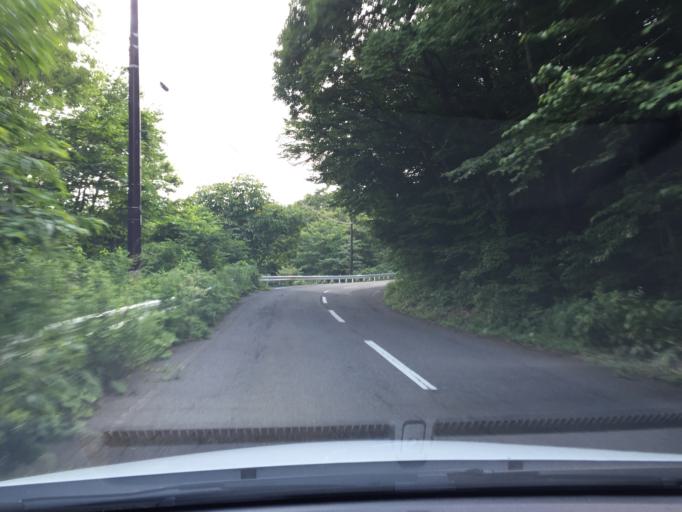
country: JP
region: Tochigi
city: Kuroiso
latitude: 37.2600
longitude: 140.0750
